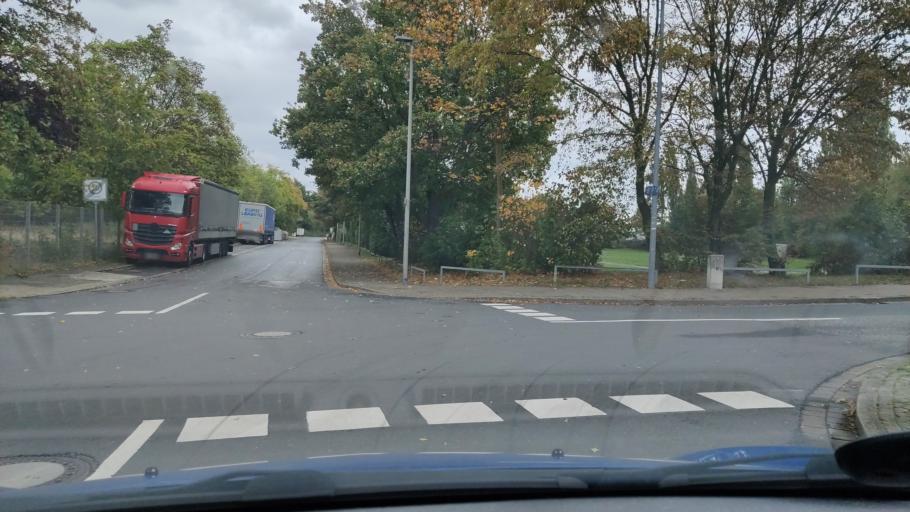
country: DE
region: Lower Saxony
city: Hannover
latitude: 52.3863
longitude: 9.6673
